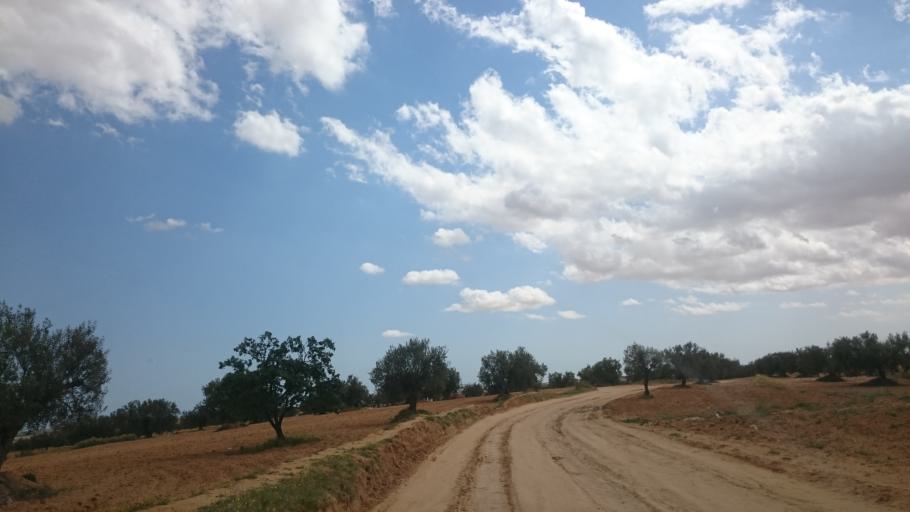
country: TN
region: Safaqis
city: Sfax
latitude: 34.7506
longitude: 10.4876
